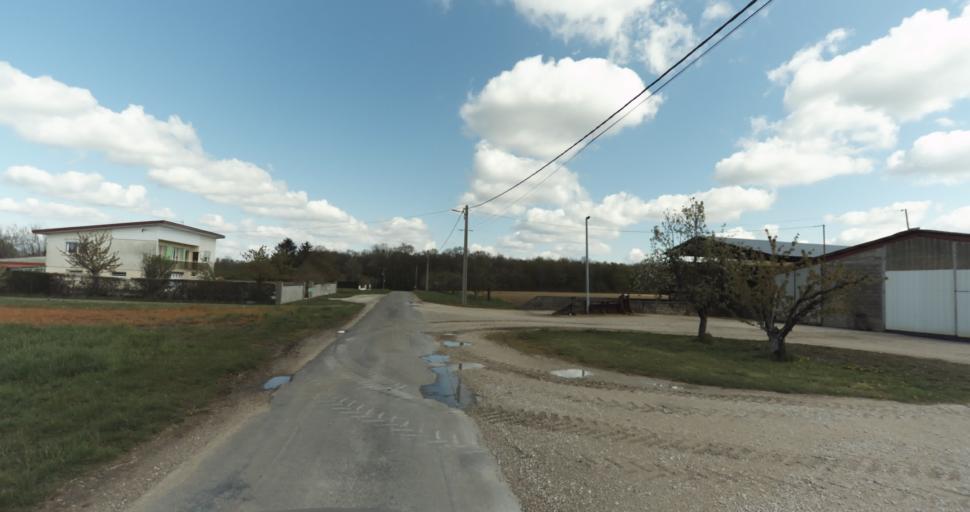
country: FR
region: Bourgogne
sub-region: Departement de la Cote-d'Or
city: Auxonne
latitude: 47.2094
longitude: 5.4321
